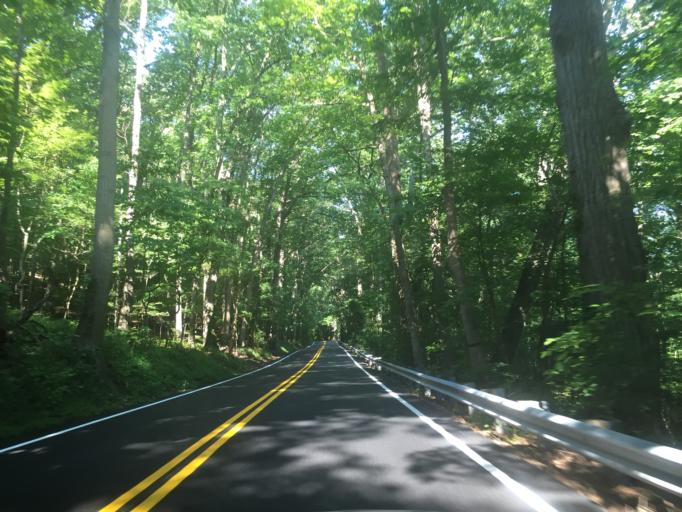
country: US
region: Maryland
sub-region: Baltimore County
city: Mays Chapel
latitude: 39.4132
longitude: -76.6838
